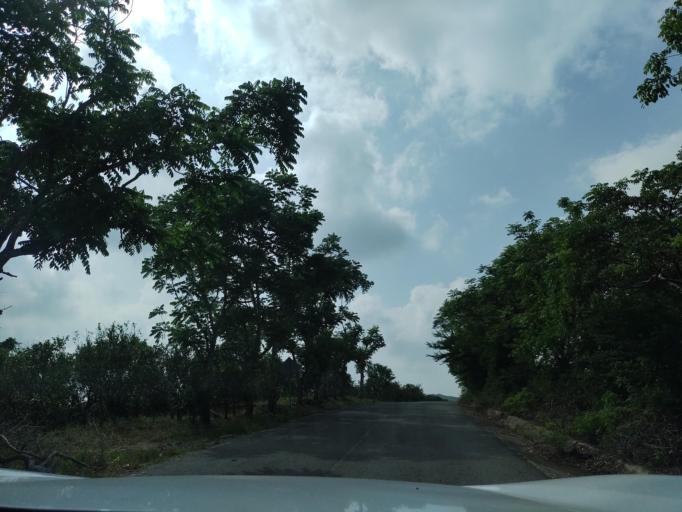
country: MX
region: Veracruz
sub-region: Martinez de la Torre
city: La Union Paso Largo
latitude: 20.2474
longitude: -97.0930
